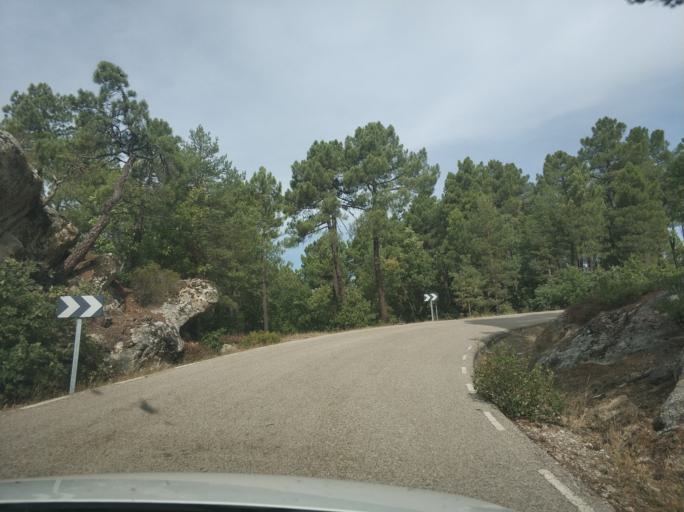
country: ES
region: Castille and Leon
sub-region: Provincia de Soria
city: Duruelo de la Sierra
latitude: 41.8945
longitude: -2.9457
